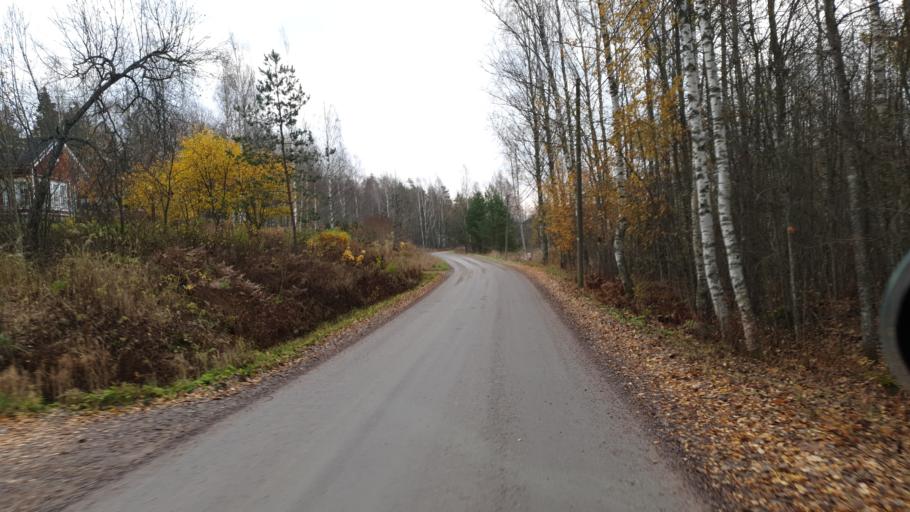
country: FI
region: Uusimaa
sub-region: Helsinki
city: Siuntio
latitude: 60.1257
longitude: 24.2815
